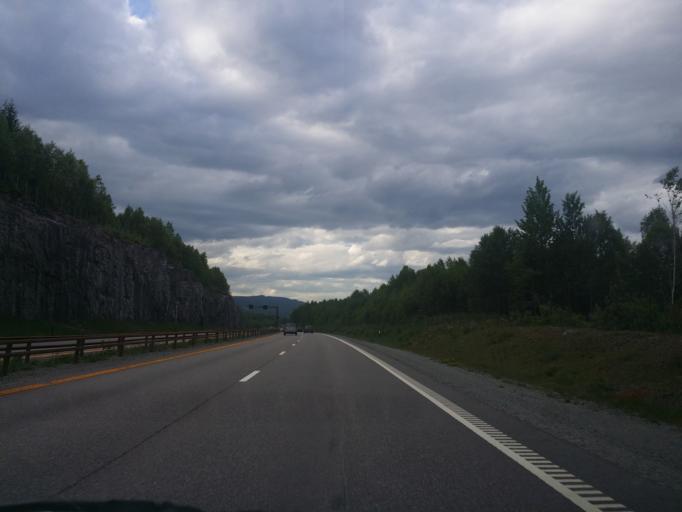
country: NO
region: Akershus
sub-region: Eidsvoll
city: Eidsvoll
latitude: 60.3520
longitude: 11.2085
